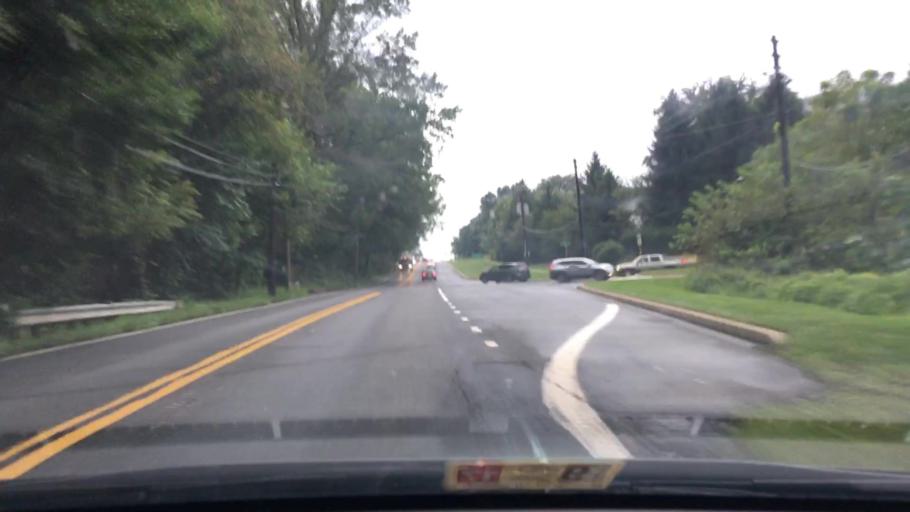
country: US
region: Maryland
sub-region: Montgomery County
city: Montgomery Village
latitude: 39.1924
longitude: -77.1524
